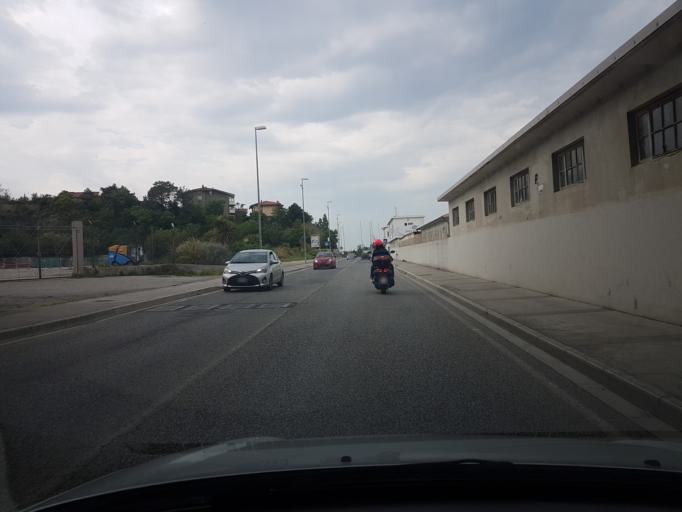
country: IT
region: Friuli Venezia Giulia
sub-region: Provincia di Trieste
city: Muggia
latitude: 45.6012
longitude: 13.7764
